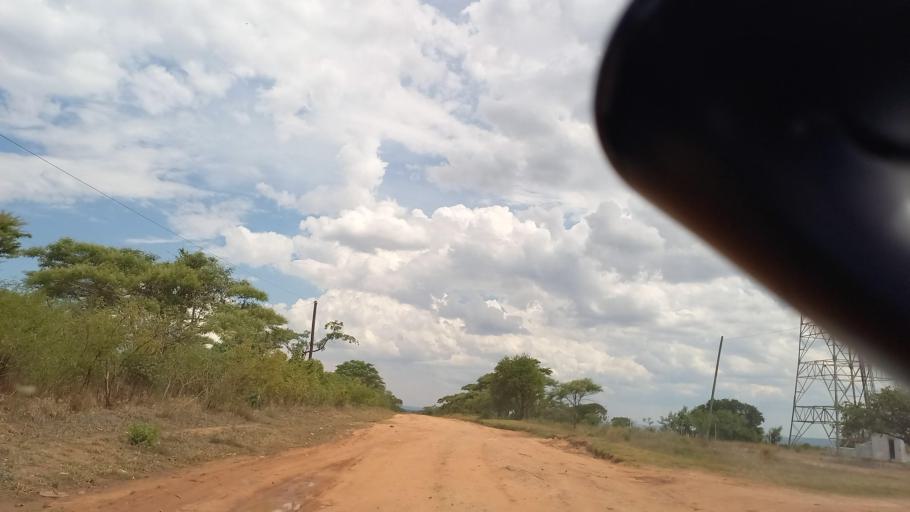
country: ZM
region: Southern
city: Nakambala
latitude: -16.0361
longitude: 27.9707
